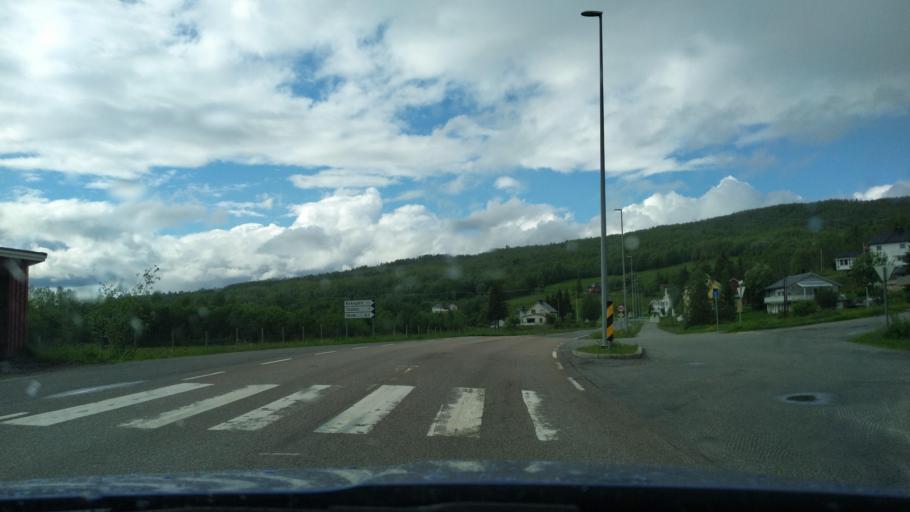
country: NO
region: Troms
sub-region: Sorreisa
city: Sorreisa
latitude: 69.1698
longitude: 18.1151
